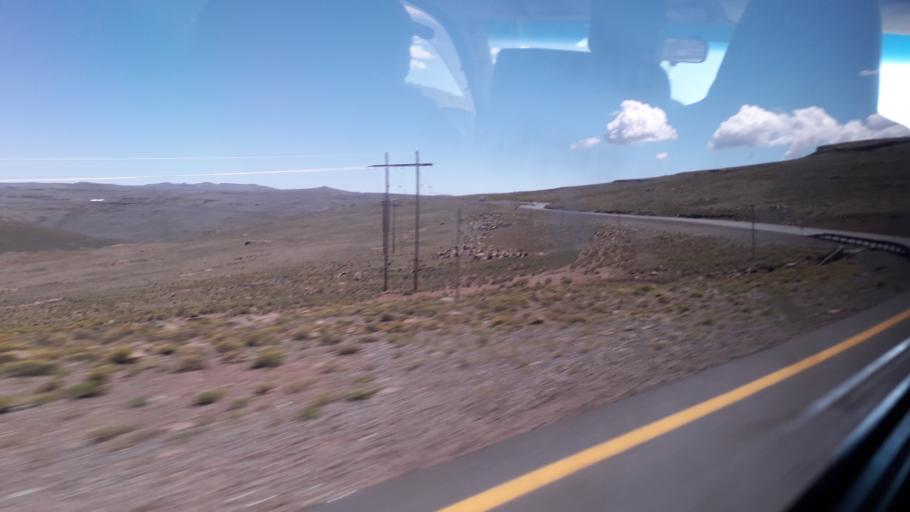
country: LS
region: Mokhotlong
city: Mokhotlong
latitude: -29.0465
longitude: 28.8593
